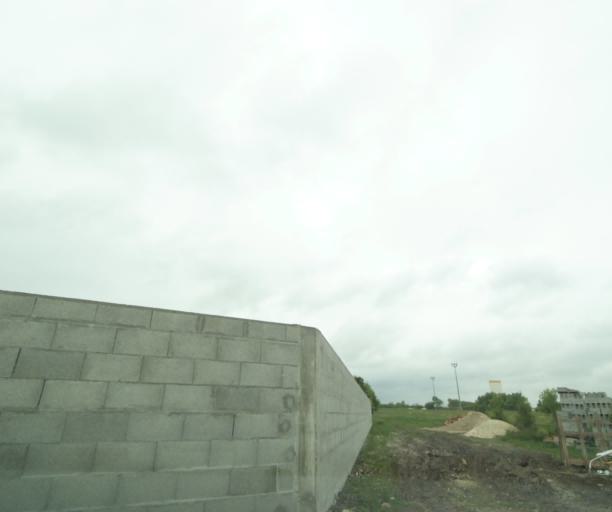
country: FR
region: Poitou-Charentes
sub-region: Departement de la Charente-Maritime
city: Perignac
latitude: 45.6545
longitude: -0.5071
